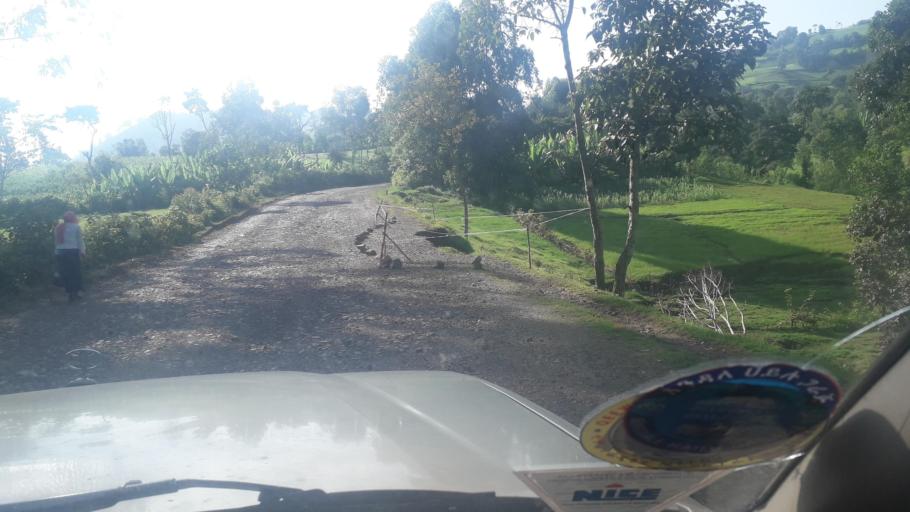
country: ET
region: Oromiya
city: Jima
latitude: 7.3857
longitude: 36.8643
